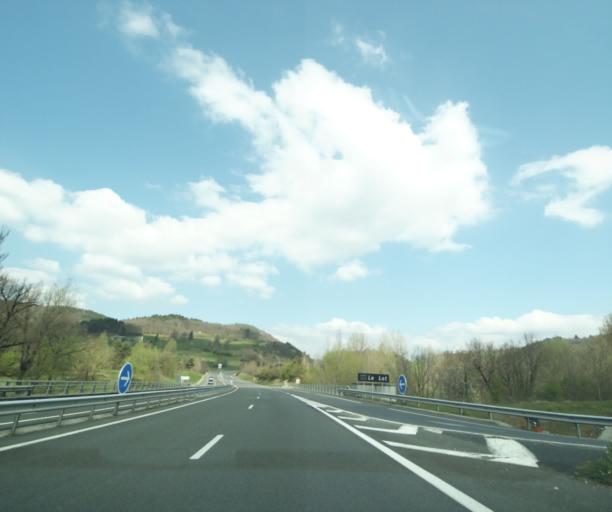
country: FR
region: Languedoc-Roussillon
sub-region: Departement de la Lozere
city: La Canourgue
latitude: 44.4384
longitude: 3.1956
